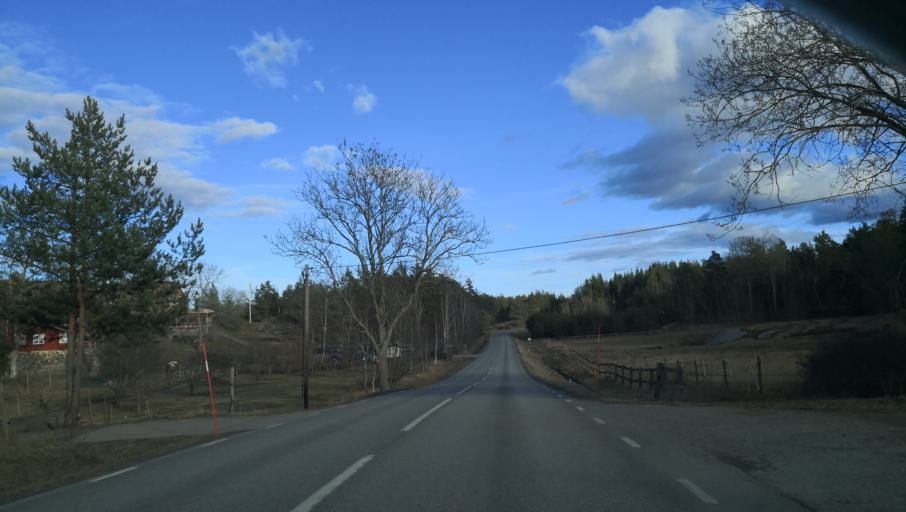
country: SE
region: Stockholm
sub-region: Varmdo Kommun
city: Gustavsberg
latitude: 59.3481
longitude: 18.3781
